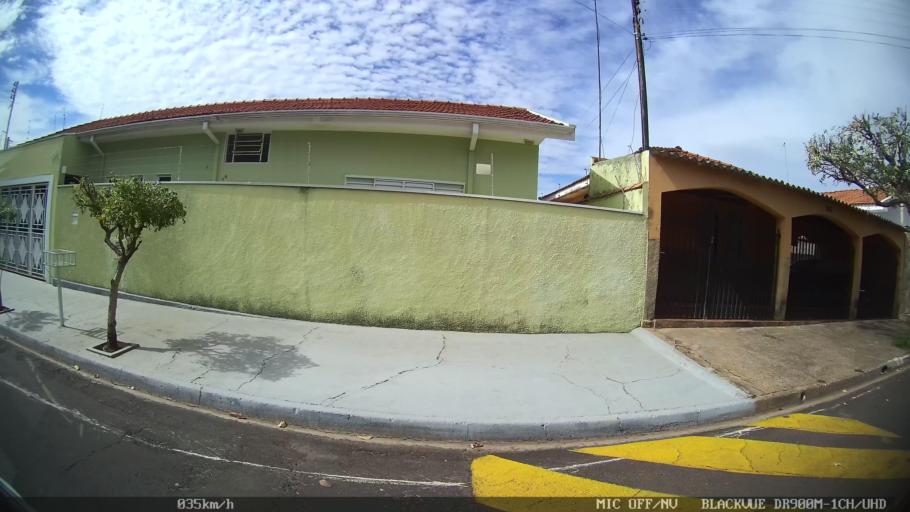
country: BR
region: Sao Paulo
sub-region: Catanduva
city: Catanduva
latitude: -21.1500
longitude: -48.9689
